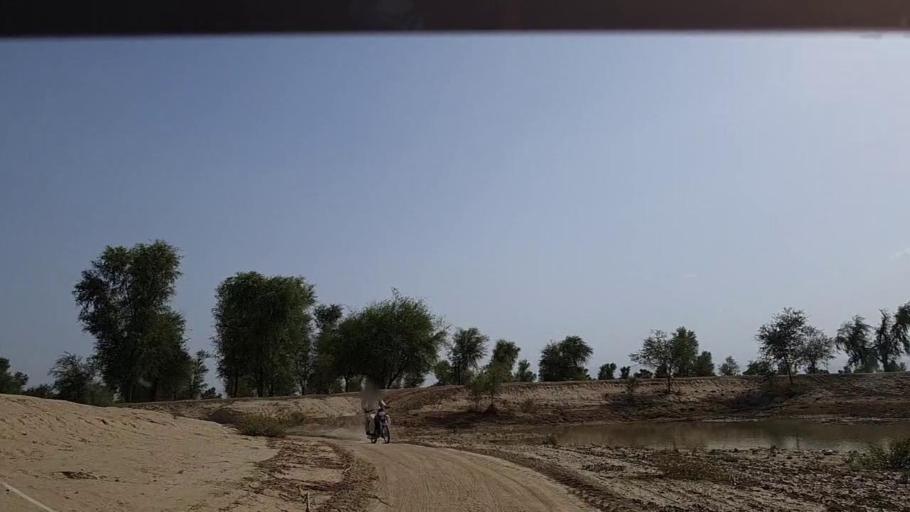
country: PK
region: Sindh
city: Johi
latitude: 26.6382
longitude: 67.5025
